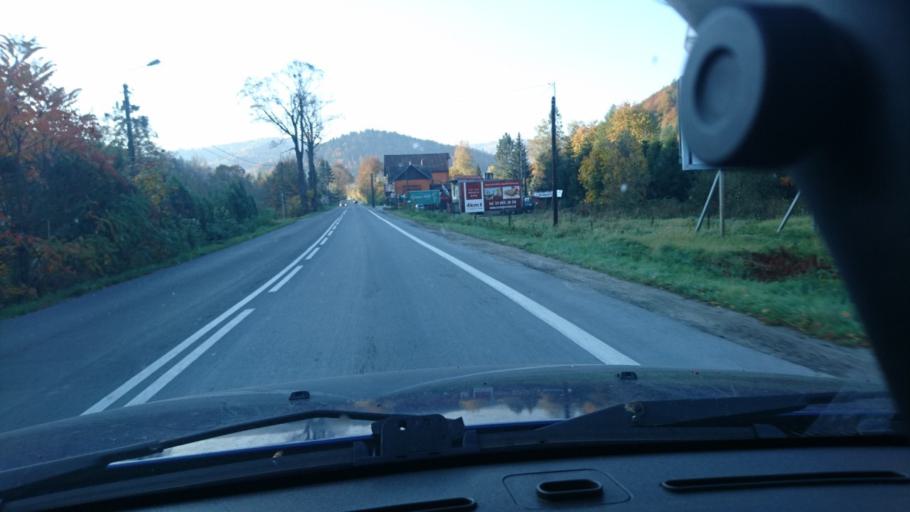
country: PL
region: Silesian Voivodeship
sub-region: Powiat cieszynski
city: Wisla
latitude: 49.6746
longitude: 18.8481
